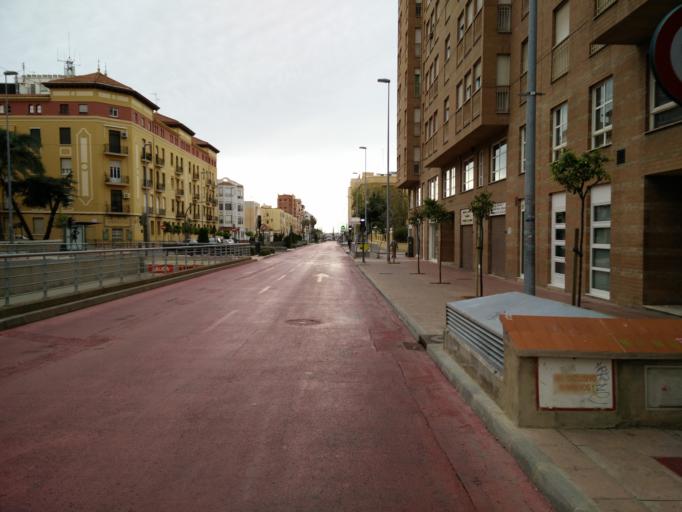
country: ES
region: Valencia
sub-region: Provincia de Castello
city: Castello de la Plana
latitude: 39.9853
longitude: -0.0325
